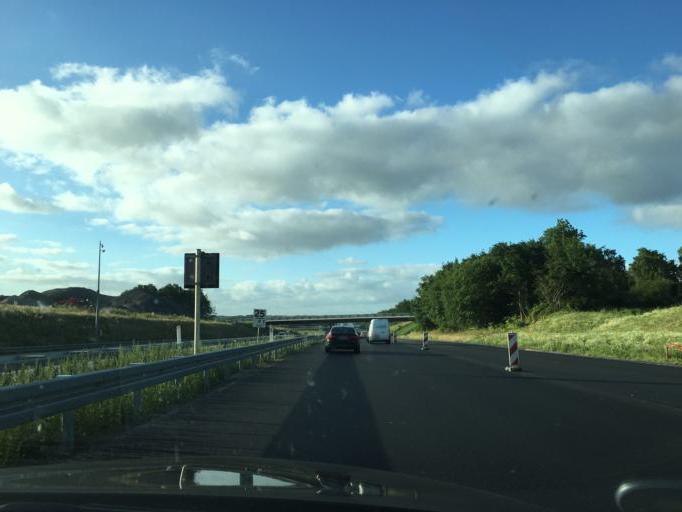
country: DK
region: Capital Region
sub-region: Horsholm Kommune
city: Horsholm
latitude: 55.8482
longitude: 12.5046
